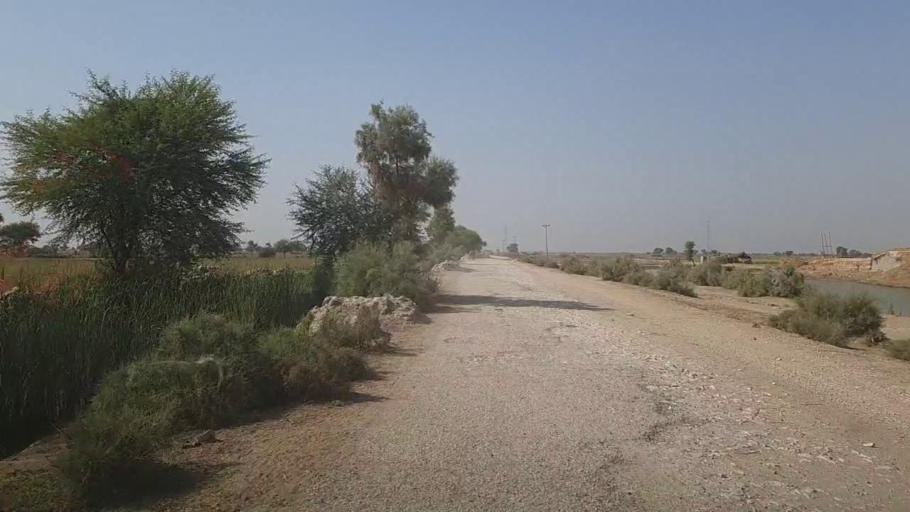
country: PK
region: Sindh
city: Kandhkot
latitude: 28.4059
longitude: 69.2536
